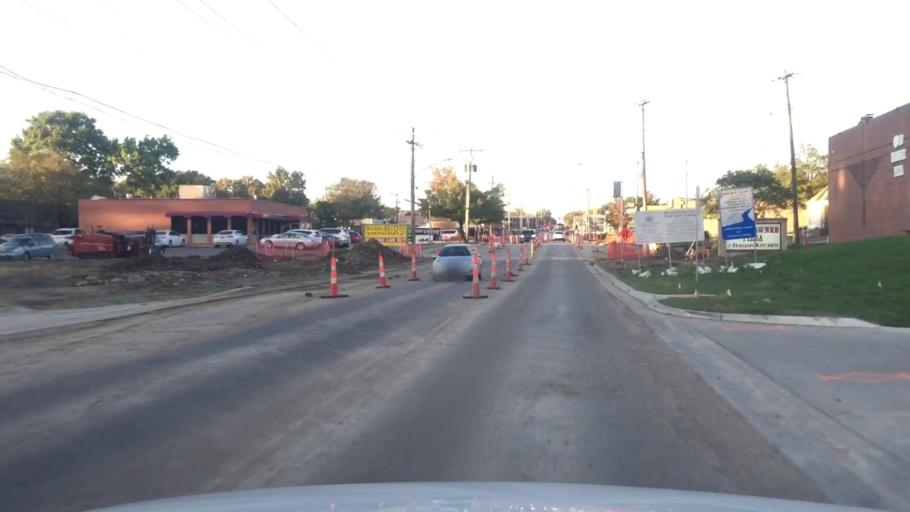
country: US
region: Kansas
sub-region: Johnson County
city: Merriam
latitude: 39.0188
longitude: -94.7146
